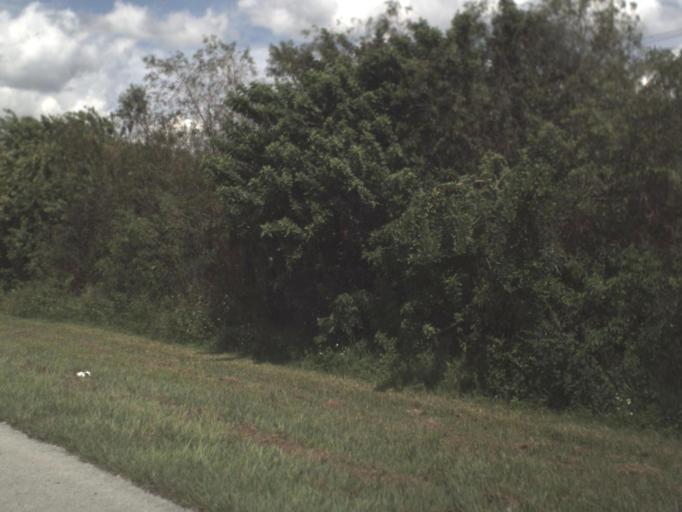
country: US
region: Florida
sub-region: Collier County
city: Immokalee
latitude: 26.4789
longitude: -81.4345
